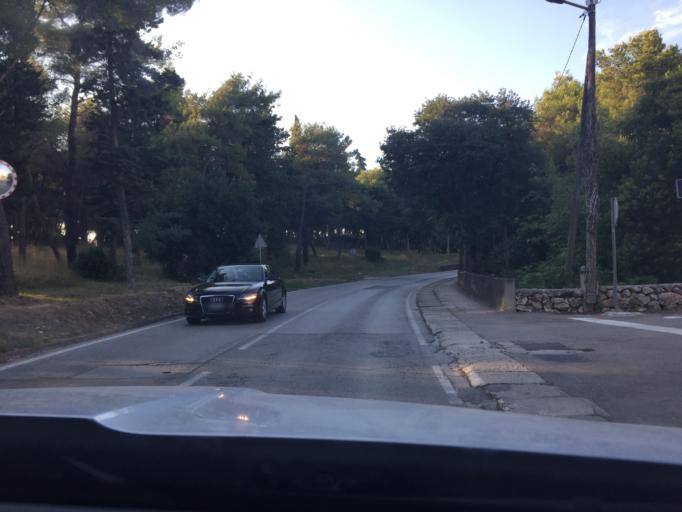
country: HR
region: Zadarska
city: Zadar
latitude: 44.1214
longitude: 15.2332
